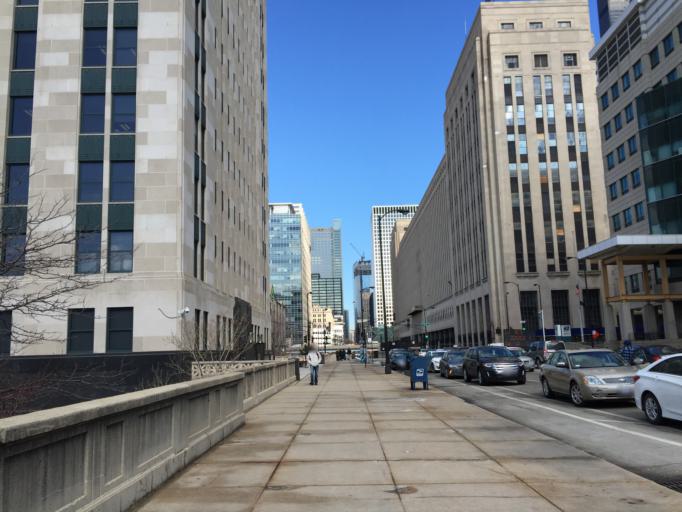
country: US
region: Illinois
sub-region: Cook County
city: Chicago
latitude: 41.8735
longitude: -87.6395
